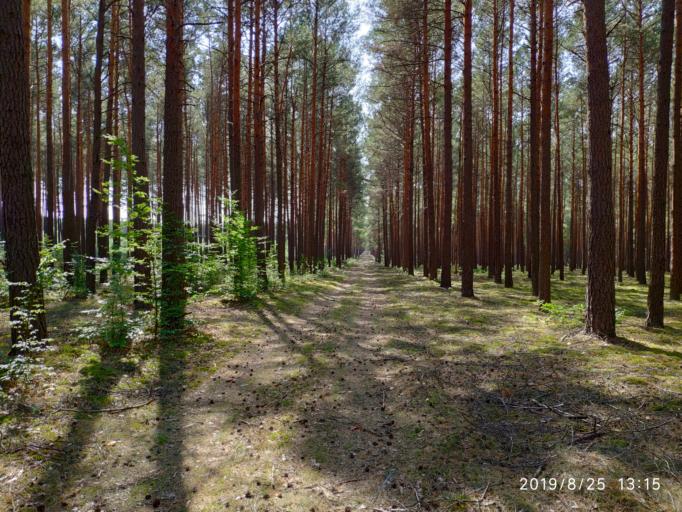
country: PL
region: Lubusz
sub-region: Powiat krosnienski
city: Dabie
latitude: 51.9930
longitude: 15.1549
